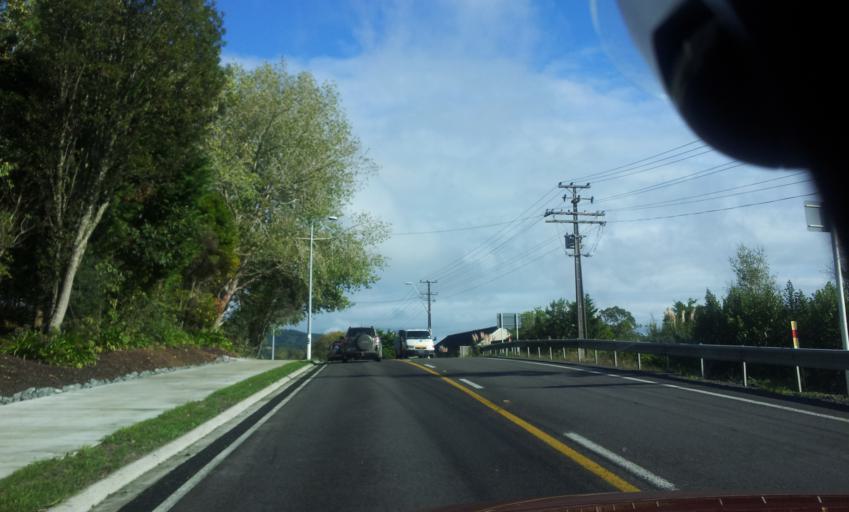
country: NZ
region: Auckland
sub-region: Auckland
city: Warkworth
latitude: -36.3934
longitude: 174.6547
